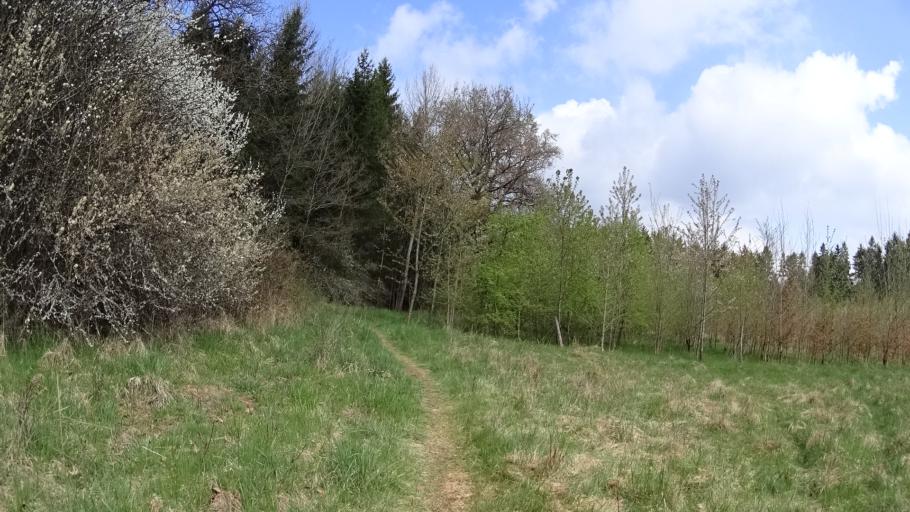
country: DE
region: Bavaria
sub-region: Upper Bavaria
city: Wettstetten
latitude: 48.8552
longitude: 11.4037
